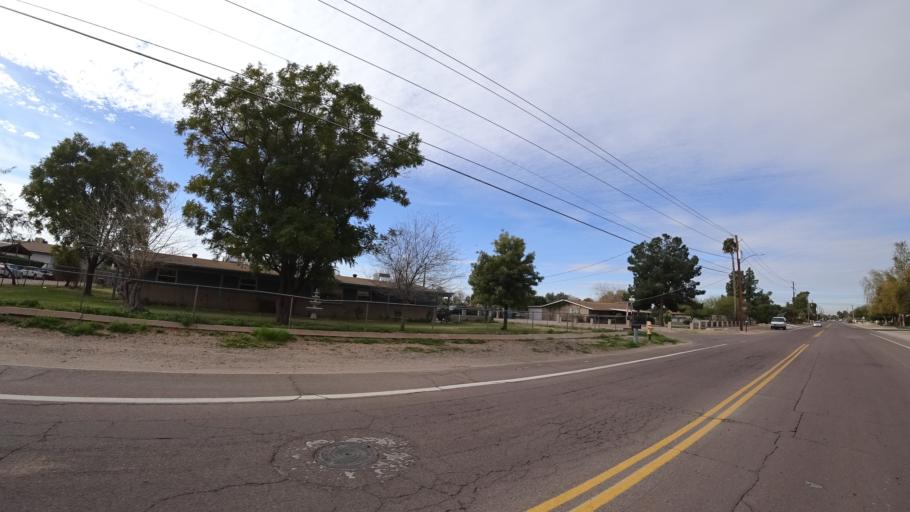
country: US
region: Arizona
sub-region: Maricopa County
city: Peoria
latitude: 33.6619
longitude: -112.1471
